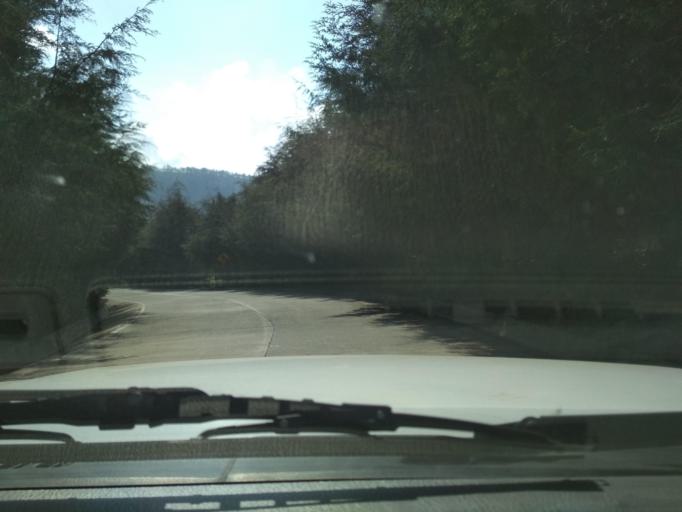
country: MX
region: Veracruz
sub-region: La Perla
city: Chilapa
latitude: 18.9930
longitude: -97.1836
